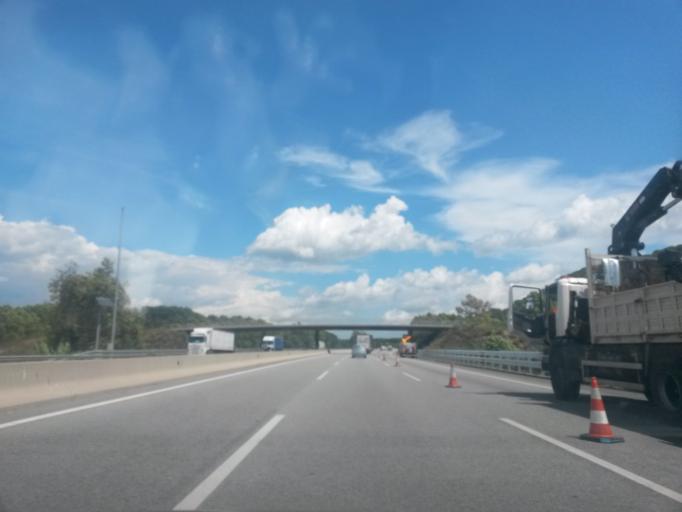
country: ES
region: Catalonia
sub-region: Provincia de Girona
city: Breda
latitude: 41.7250
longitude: 2.5850
